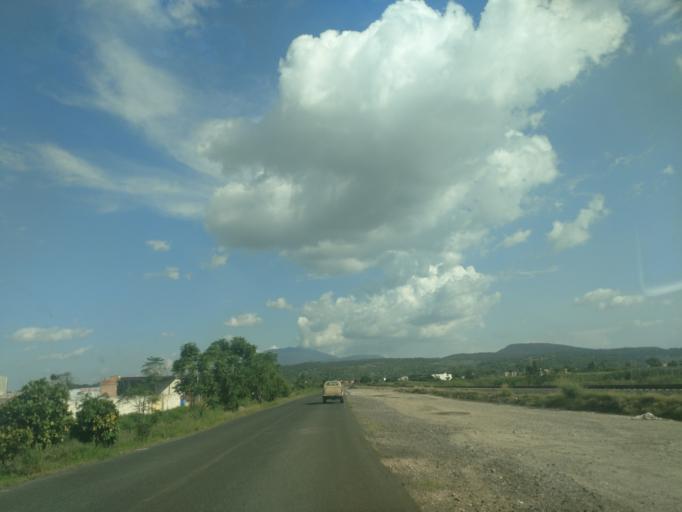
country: MX
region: Jalisco
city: Antonio Escobedo
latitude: 20.9095
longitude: -103.9892
